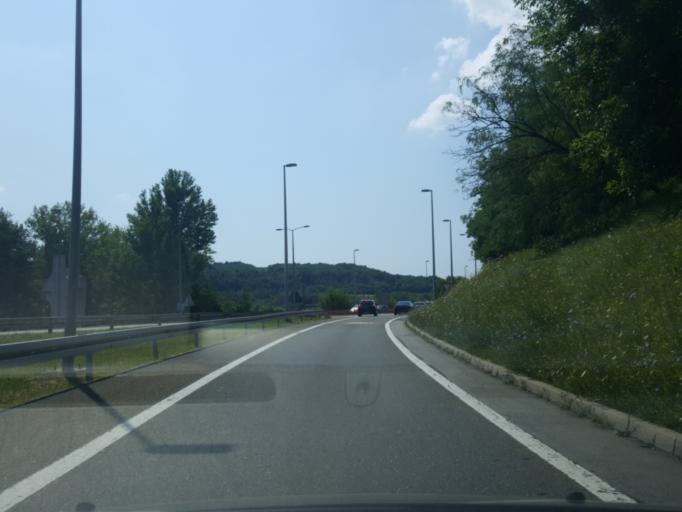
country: RS
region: Central Serbia
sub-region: Belgrade
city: Sopot
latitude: 44.5648
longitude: 20.6689
